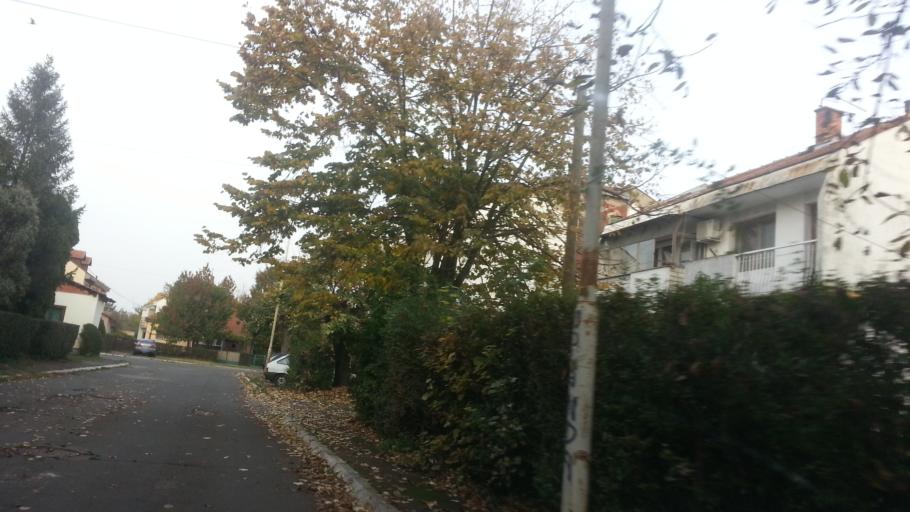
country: RS
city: Novi Banovci
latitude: 44.8942
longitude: 20.2848
